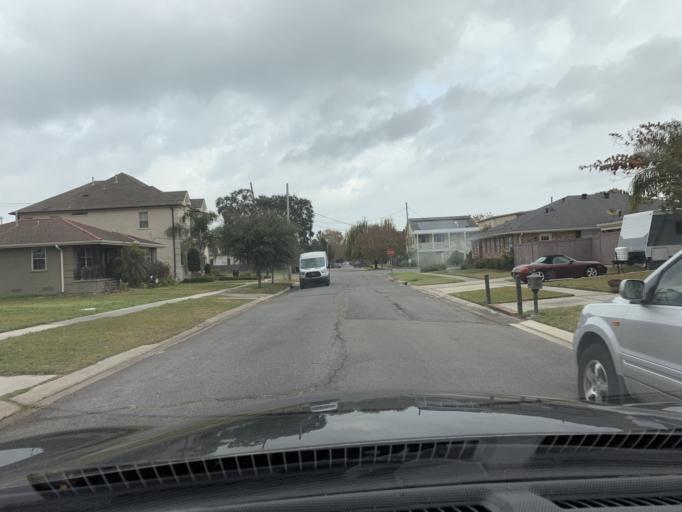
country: US
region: Louisiana
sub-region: Jefferson Parish
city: Metairie
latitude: 30.0110
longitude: -90.1008
